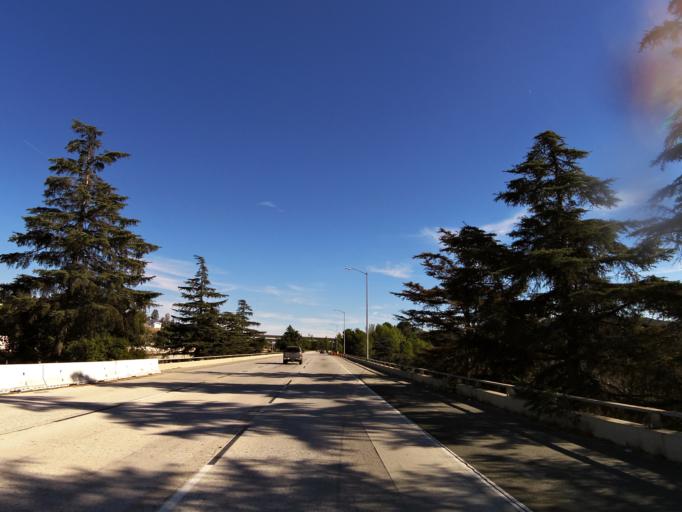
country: US
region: California
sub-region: Los Angeles County
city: La Crescenta-Montrose
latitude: 34.2098
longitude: -118.2240
